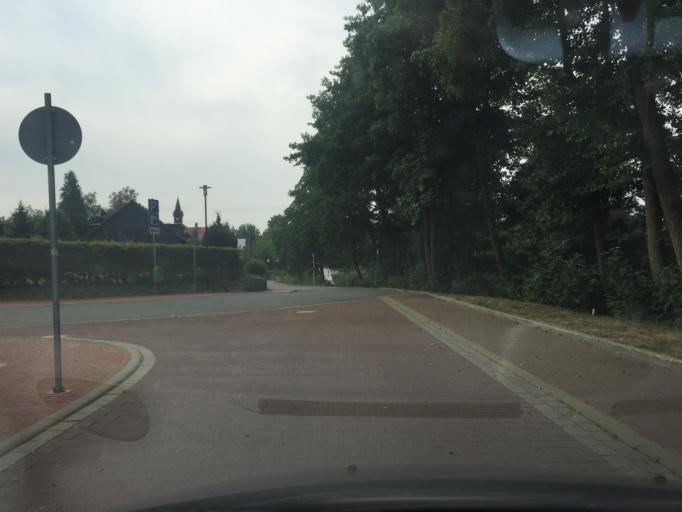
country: DE
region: Lower Saxony
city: Braunlage
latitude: 51.7296
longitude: 10.6124
